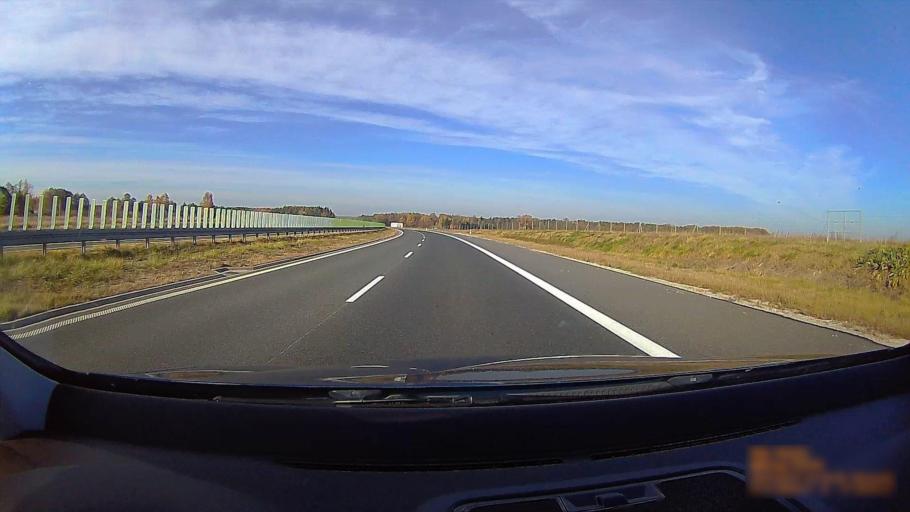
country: PL
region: Greater Poland Voivodeship
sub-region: Powiat ostrowski
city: Ostrow Wielkopolski
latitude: 51.6451
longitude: 17.8756
